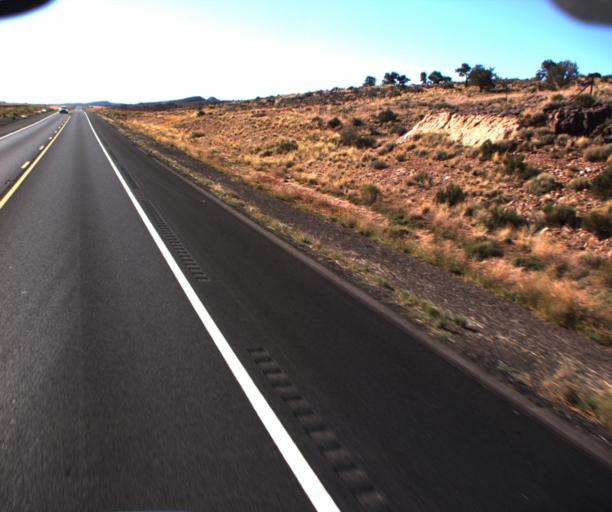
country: US
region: Arizona
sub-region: Coconino County
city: LeChee
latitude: 36.5023
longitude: -111.5823
